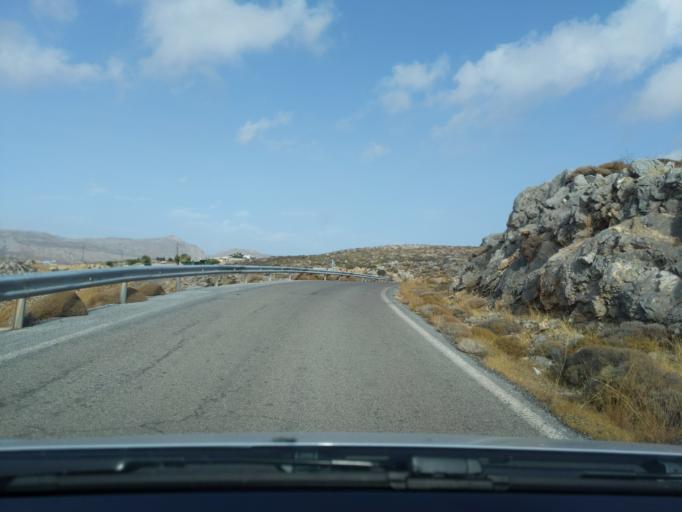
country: GR
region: Crete
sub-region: Nomos Lasithiou
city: Palekastro
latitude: 35.0843
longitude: 26.2585
